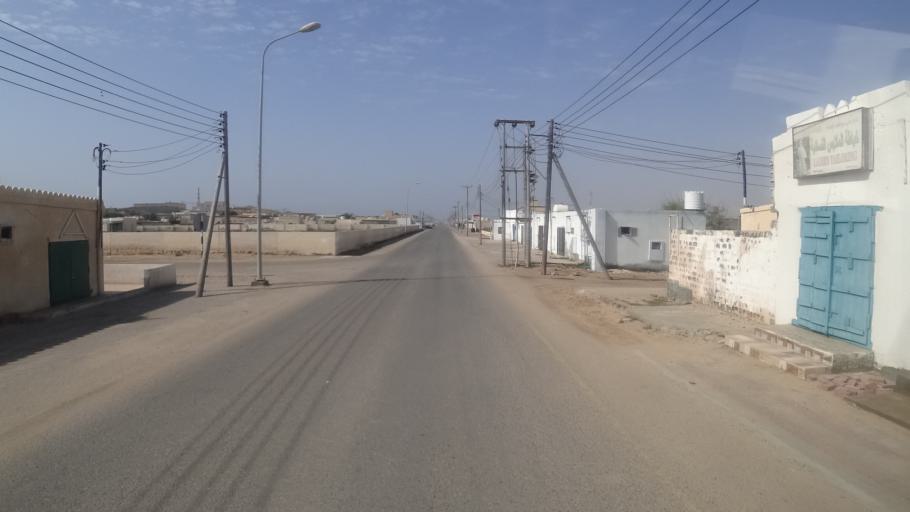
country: OM
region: Ash Sharqiyah
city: Sur
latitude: 22.1821
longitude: 59.7632
